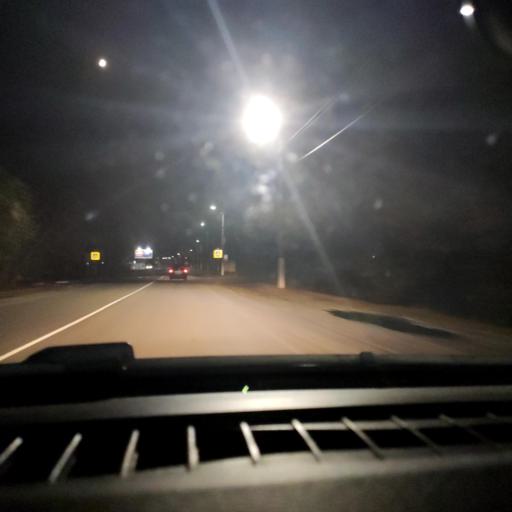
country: RU
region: Voronezj
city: Novaya Usman'
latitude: 51.6230
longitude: 39.3977
